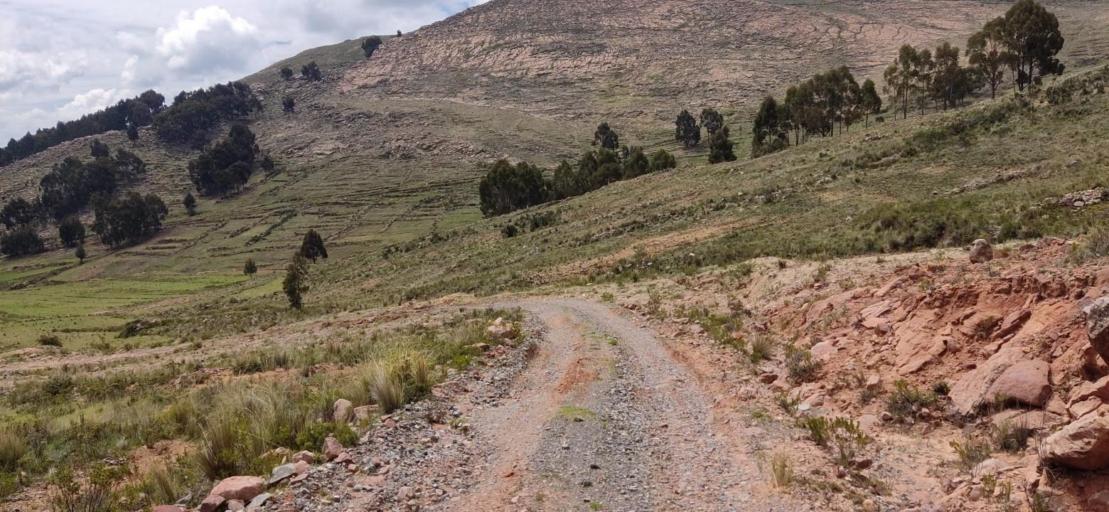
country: BO
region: La Paz
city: Batallas
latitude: -16.3438
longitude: -68.6480
